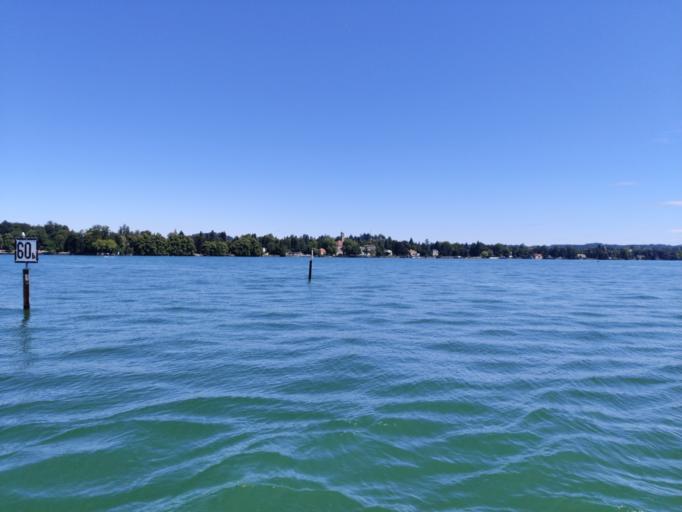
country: DE
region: Bavaria
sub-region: Swabia
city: Bodolz
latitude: 47.5502
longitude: 9.6581
